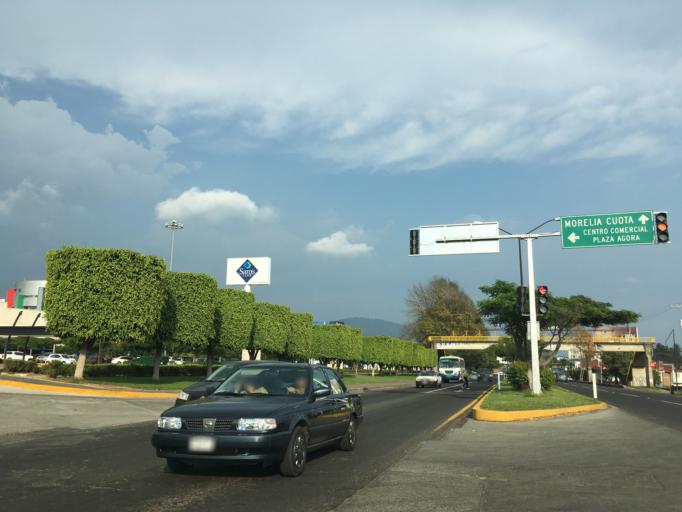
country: MX
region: Michoacan
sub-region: Uruapan
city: Uruapan
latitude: 19.4217
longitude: -102.0391
